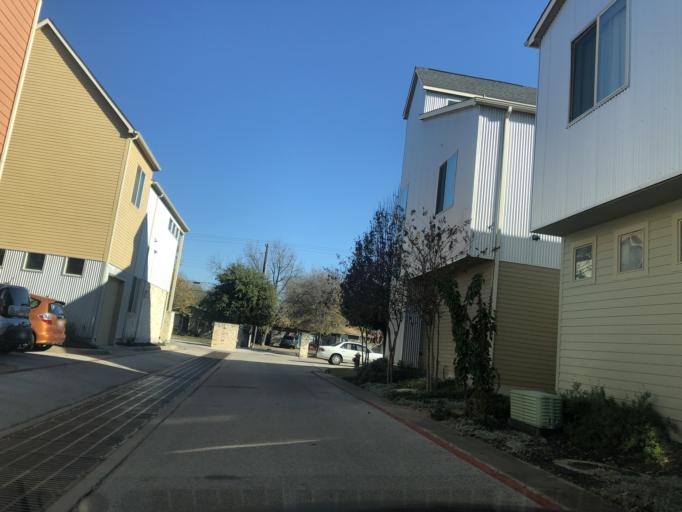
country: US
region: Texas
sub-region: Travis County
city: Austin
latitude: 30.3273
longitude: -97.7376
